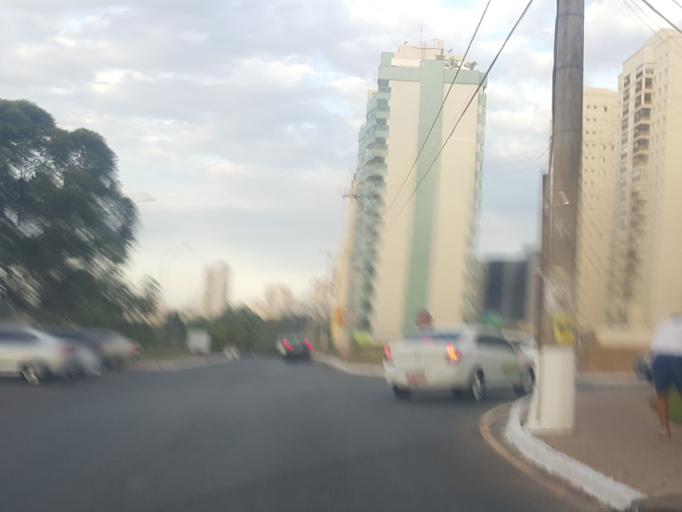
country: BR
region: Federal District
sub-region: Brasilia
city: Brasilia
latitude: -15.8346
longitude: -48.0304
